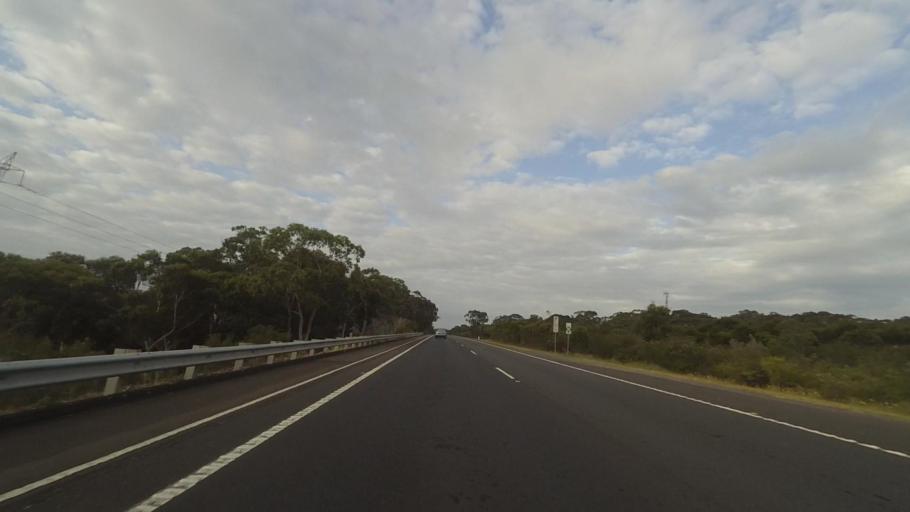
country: AU
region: New South Wales
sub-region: Wollongong
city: Bulli
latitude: -34.2604
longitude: 150.9294
